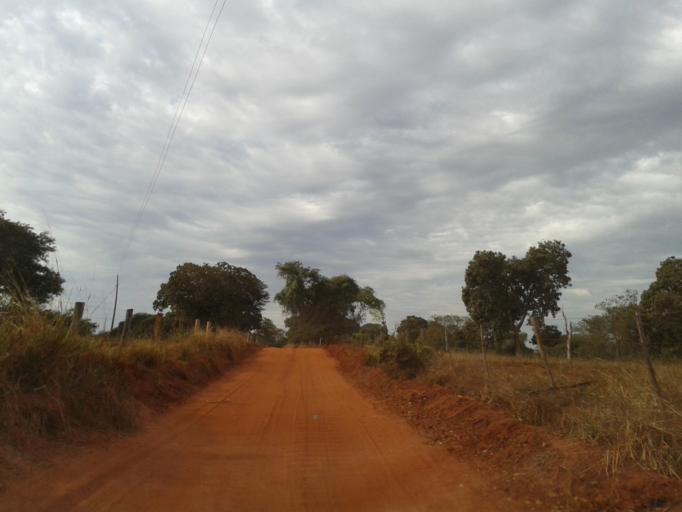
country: BR
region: Minas Gerais
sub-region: Santa Vitoria
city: Santa Vitoria
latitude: -18.7639
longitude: -50.1894
